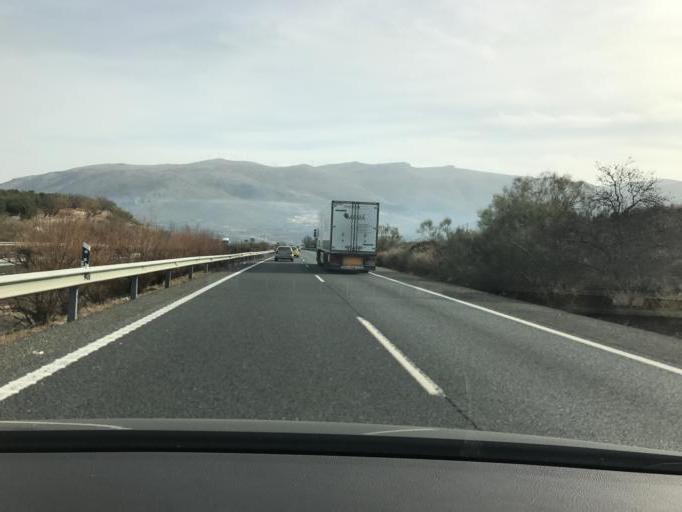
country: ES
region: Andalusia
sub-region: Provincia de Malaga
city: Villanueva de Tapia
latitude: 37.1461
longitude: -4.2472
